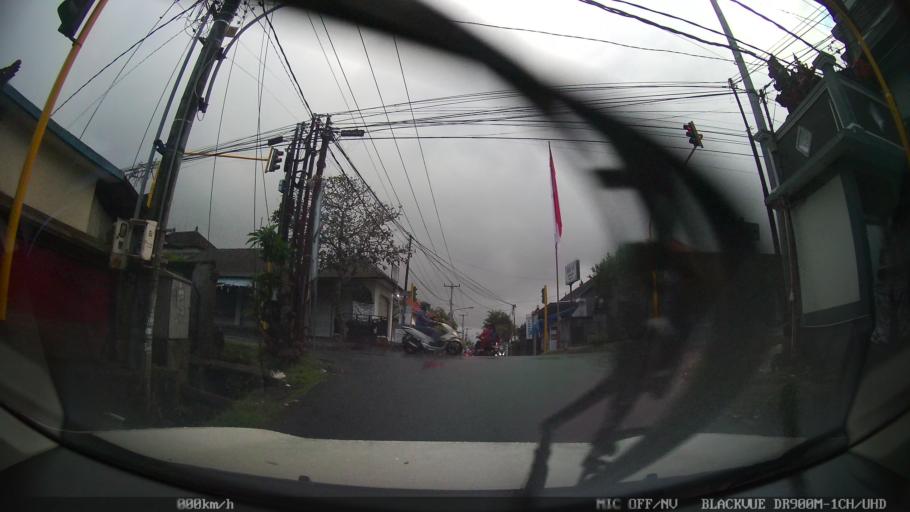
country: ID
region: Bali
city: Banjar Batur
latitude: -8.5990
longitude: 115.2188
